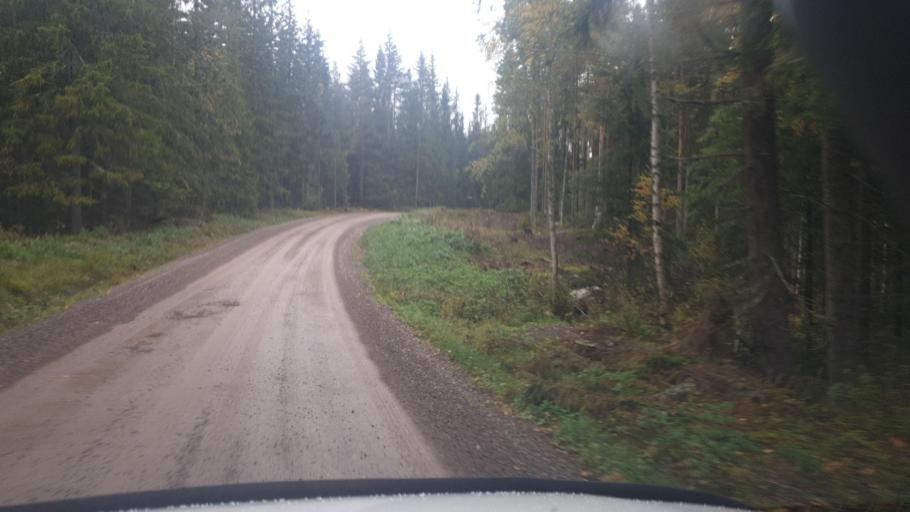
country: SE
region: Vaermland
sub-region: Arvika Kommun
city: Arvika
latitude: 59.9632
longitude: 12.6576
